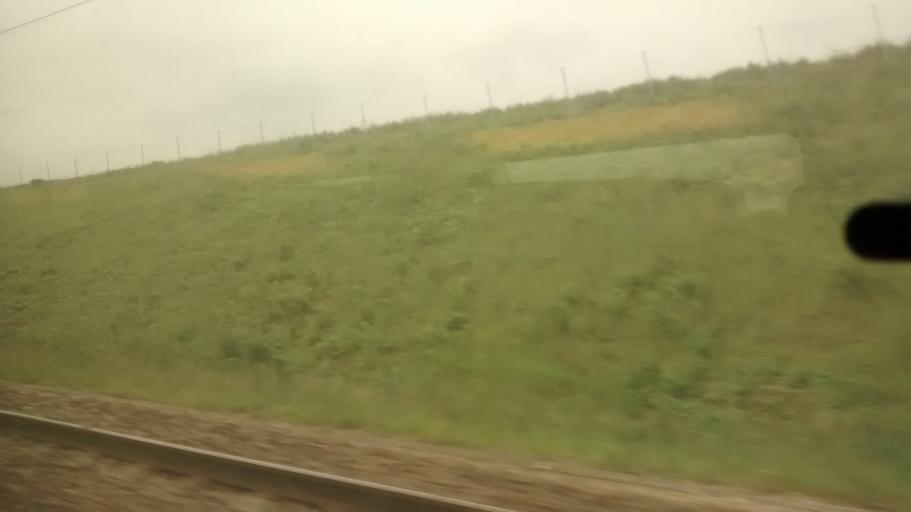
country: FR
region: Ile-de-France
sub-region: Departement de Seine-et-Marne
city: Moisenay
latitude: 48.5586
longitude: 2.7664
